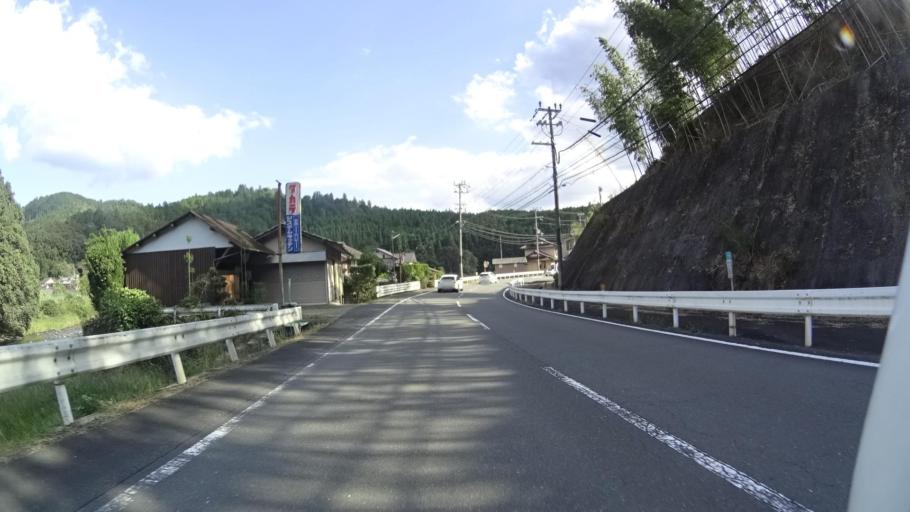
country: JP
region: Kyoto
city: Kameoka
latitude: 35.1828
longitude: 135.5144
